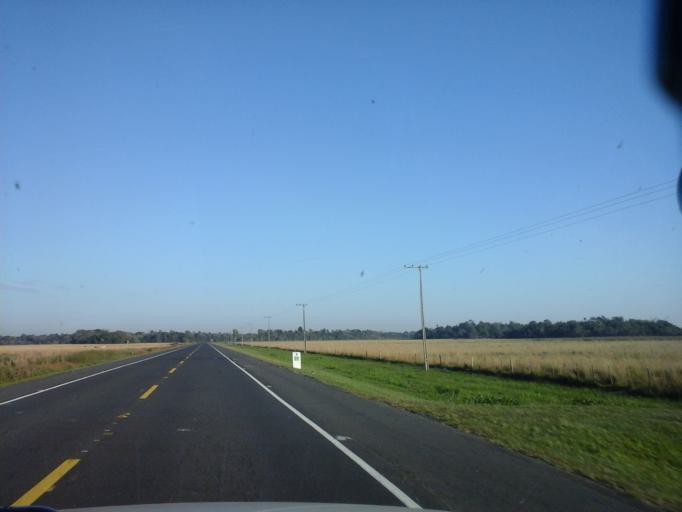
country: PY
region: Neembucu
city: Pilar
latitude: -26.8611
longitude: -57.9488
